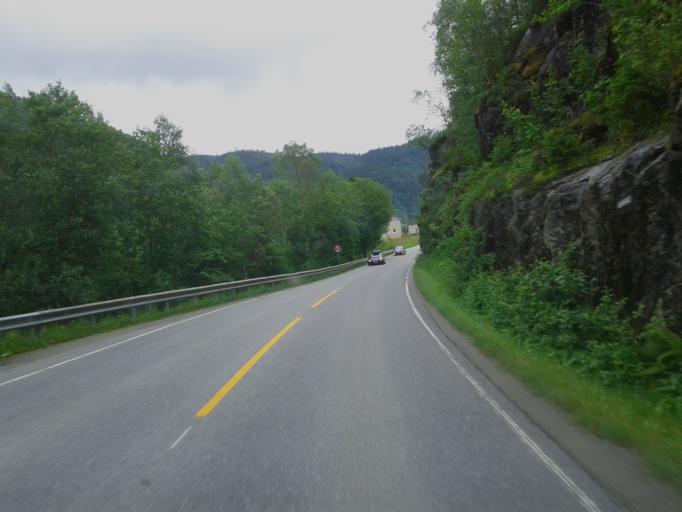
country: NO
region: Sor-Trondelag
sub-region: Midtre Gauldal
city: Storen
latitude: 63.0182
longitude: 10.4125
